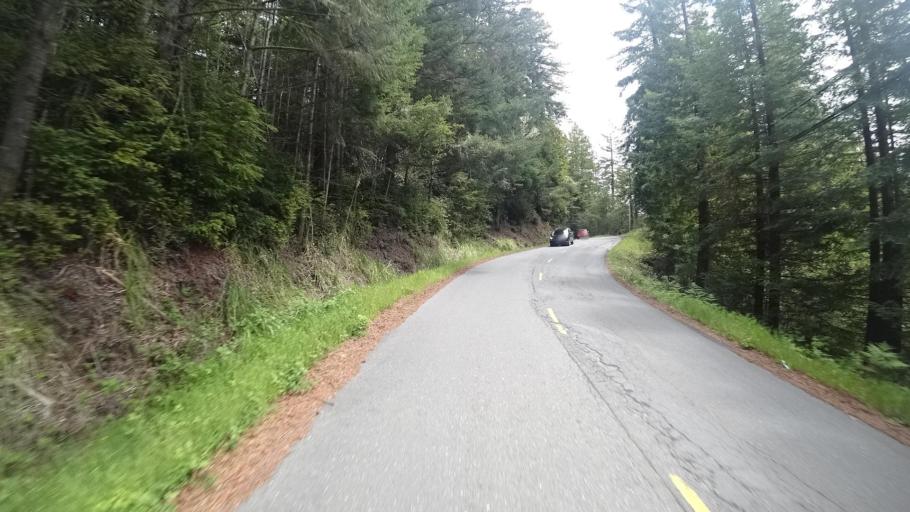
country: US
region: California
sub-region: Humboldt County
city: Bayside
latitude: 40.7870
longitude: -124.0641
